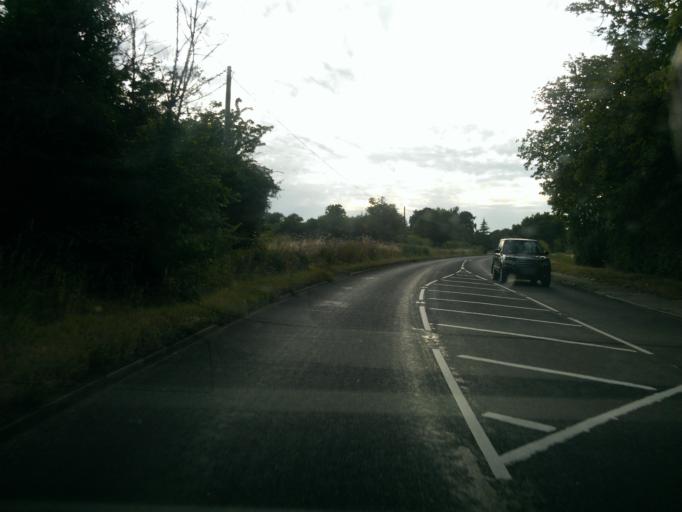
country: GB
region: England
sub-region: Essex
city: Alresford
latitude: 51.8680
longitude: 1.0264
